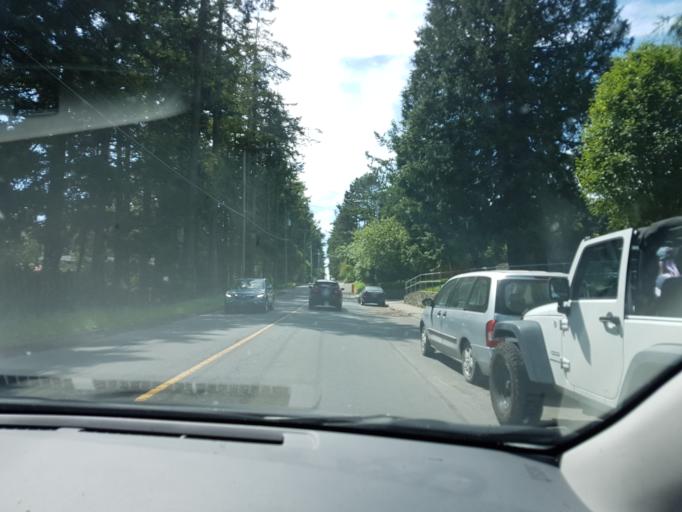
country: CA
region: British Columbia
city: Oak Bay
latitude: 48.4803
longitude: -123.3061
